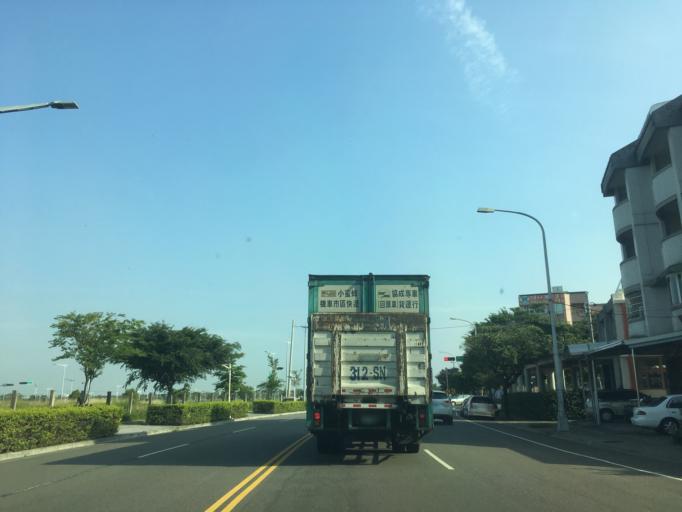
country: TW
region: Taiwan
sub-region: Taichung City
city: Taichung
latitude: 24.1928
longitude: 120.6766
